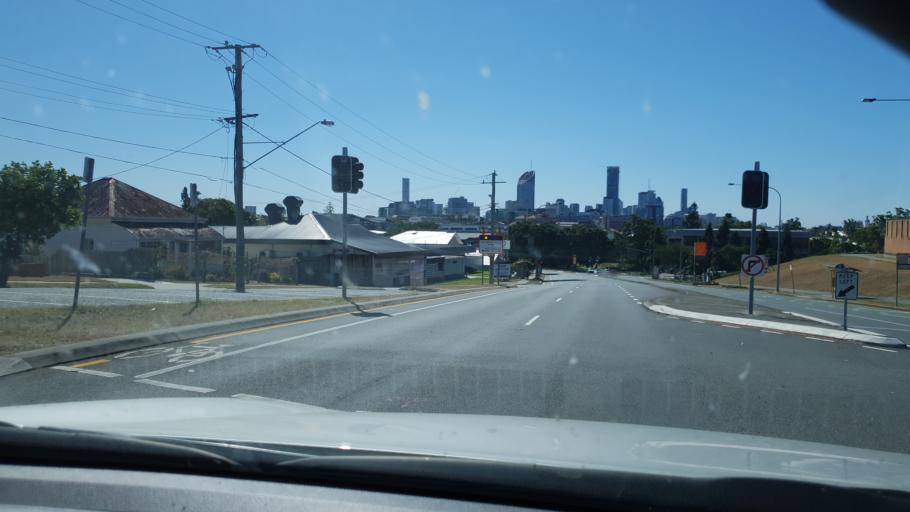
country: AU
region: Queensland
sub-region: Brisbane
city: Woolloongabba
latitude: -27.4961
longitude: 153.0279
